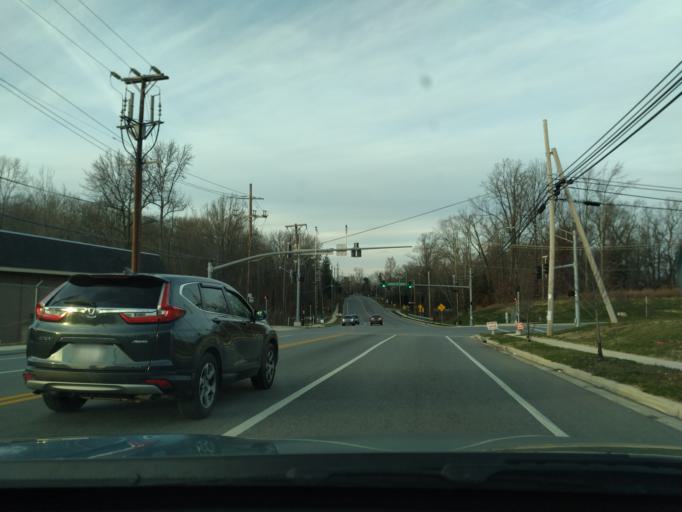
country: US
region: Maryland
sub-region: Prince George's County
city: Clinton
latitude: 38.7561
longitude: -76.8949
